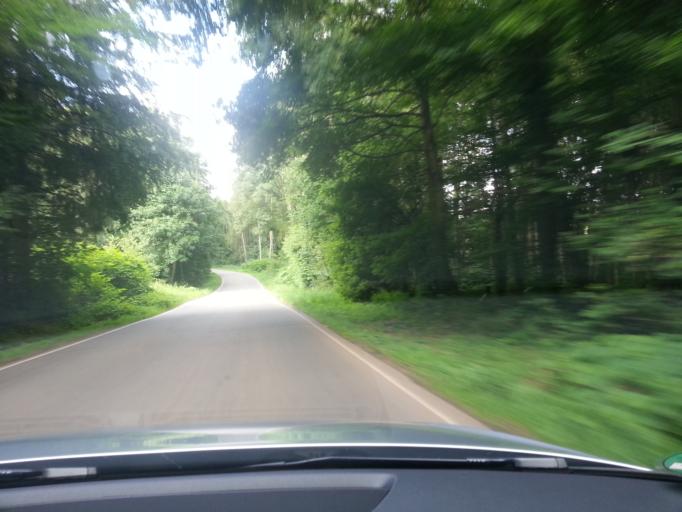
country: DE
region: Saarland
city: Orscholz
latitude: 49.5241
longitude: 6.5224
